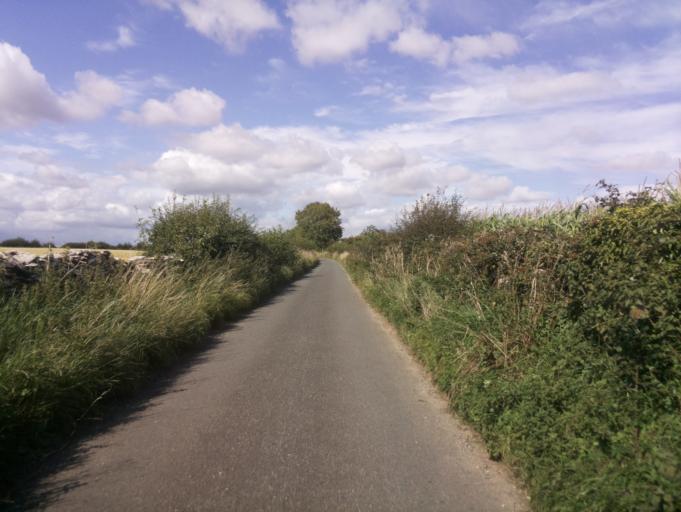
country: GB
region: England
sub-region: Gloucestershire
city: Tetbury
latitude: 51.6337
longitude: -2.1742
